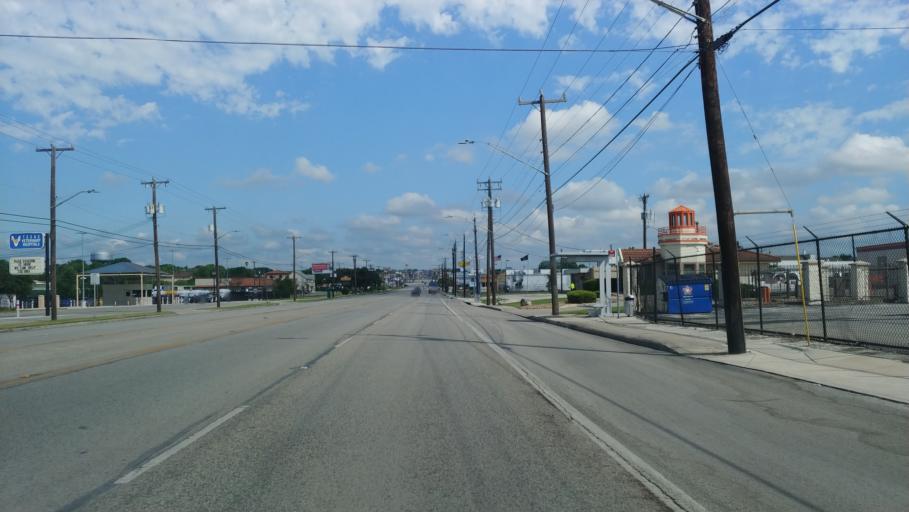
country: US
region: Texas
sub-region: Bexar County
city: Balcones Heights
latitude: 29.4755
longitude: -98.5369
